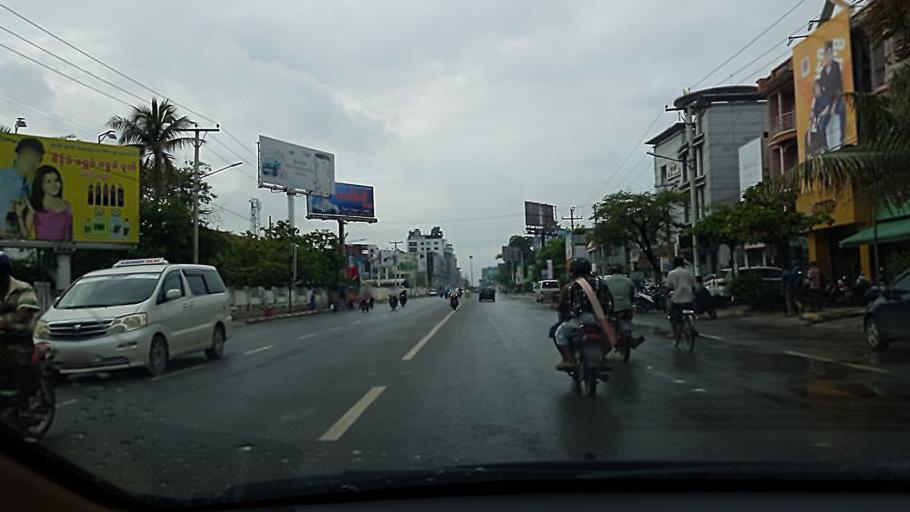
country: MM
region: Mandalay
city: Mandalay
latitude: 21.9808
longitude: 96.0871
